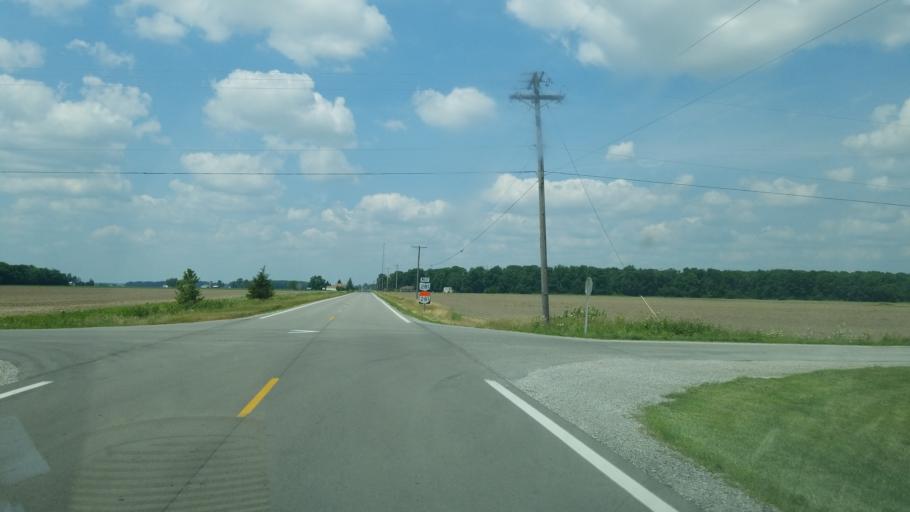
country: US
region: Ohio
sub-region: Henry County
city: Holgate
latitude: 41.2821
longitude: -84.1906
